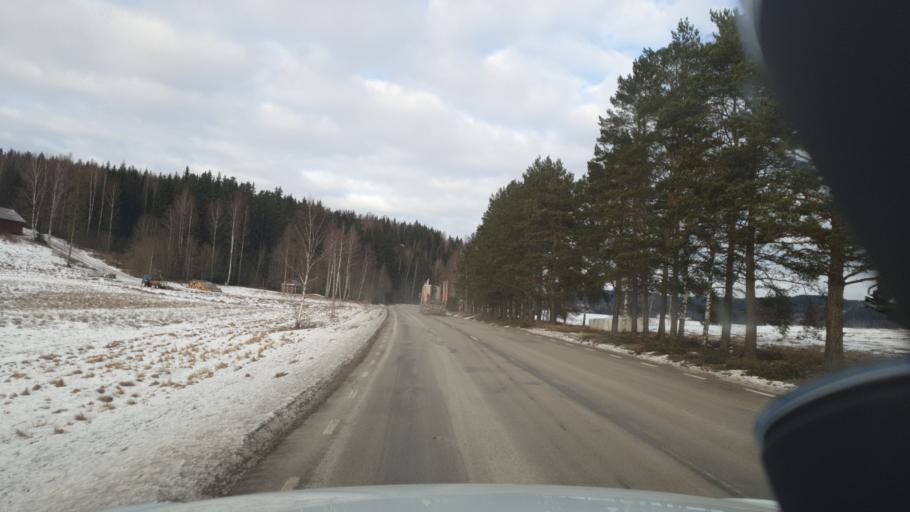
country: SE
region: Vaermland
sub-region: Arvika Kommun
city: Arvika
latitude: 59.7033
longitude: 12.6366
